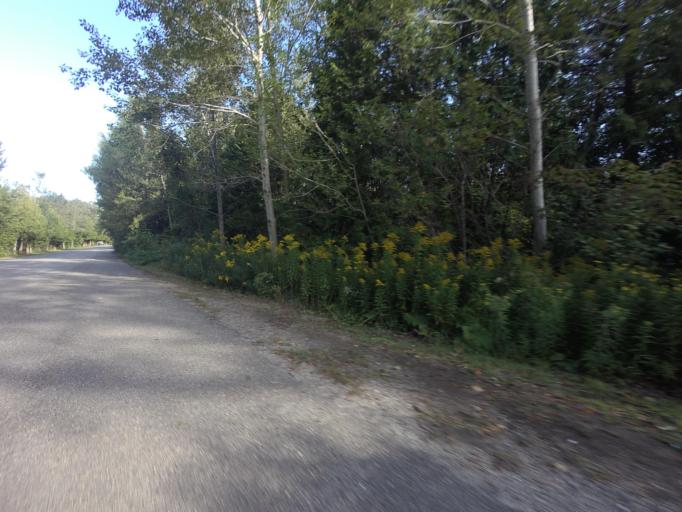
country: CA
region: Ontario
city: Waterloo
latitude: 43.6707
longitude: -80.4431
